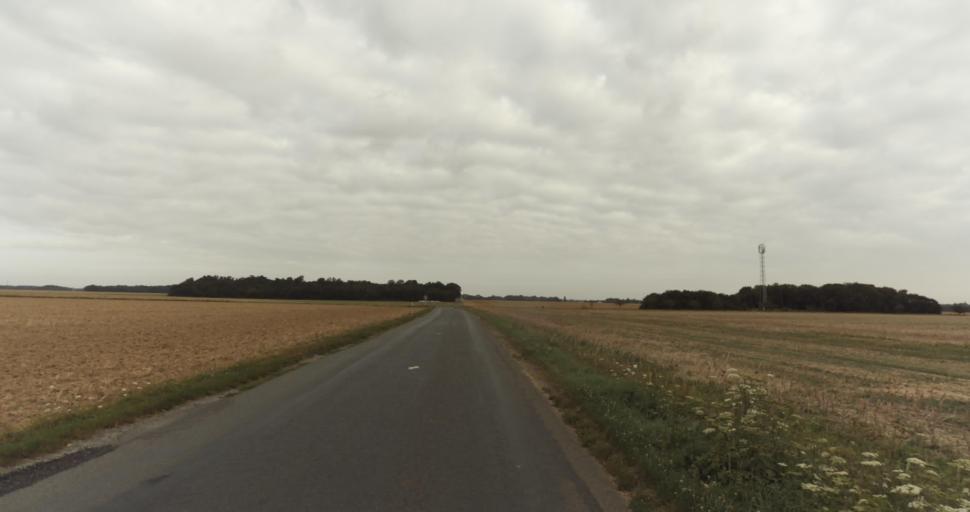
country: FR
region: Haute-Normandie
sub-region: Departement de l'Eure
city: Saint-Germain-sur-Avre
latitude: 48.8047
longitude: 1.2720
